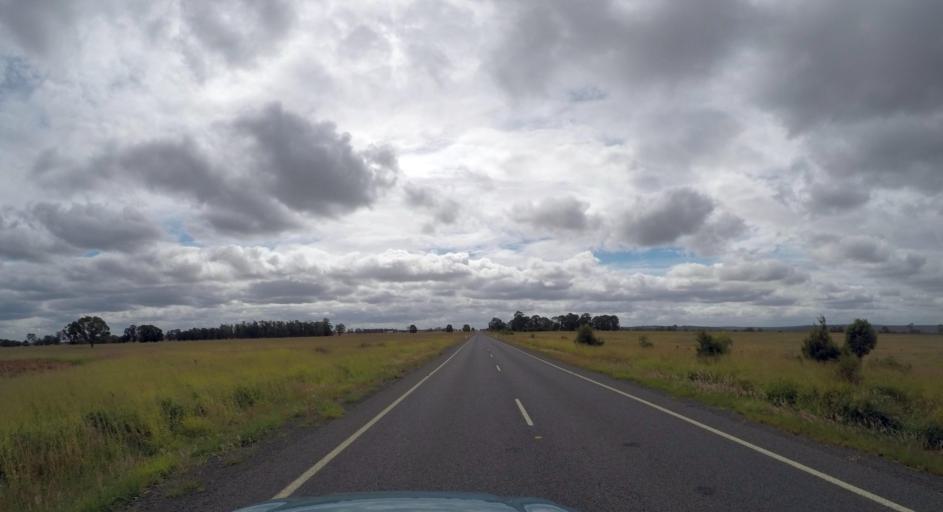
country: AU
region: Queensland
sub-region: South Burnett
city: Kingaroy
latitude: -26.3874
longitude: 151.2449
